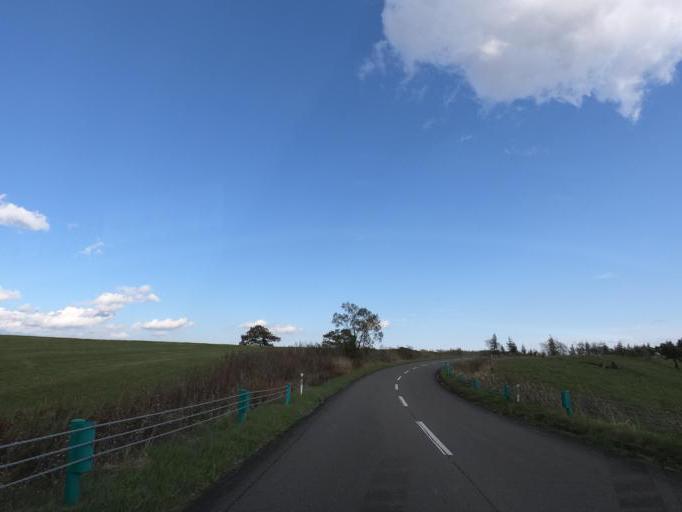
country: JP
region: Hokkaido
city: Otofuke
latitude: 43.2773
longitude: 143.2327
